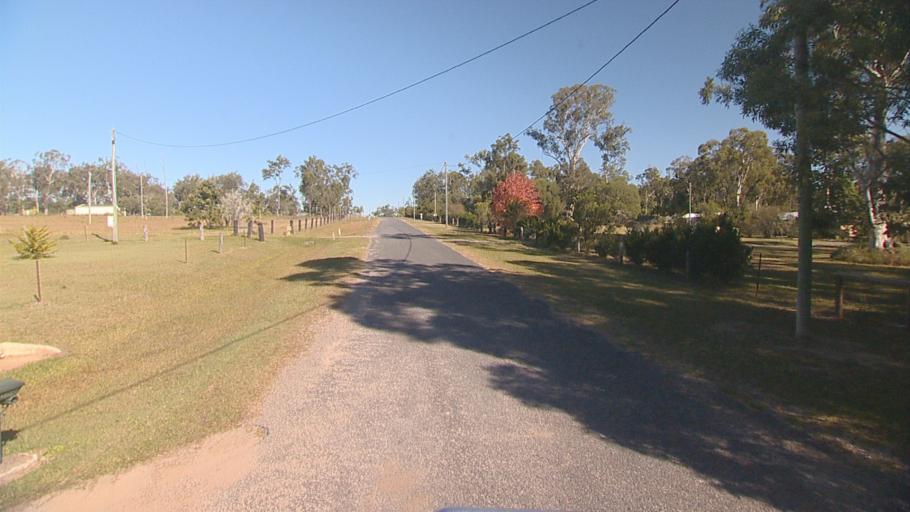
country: AU
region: Queensland
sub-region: Logan
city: Logan Reserve
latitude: -27.7255
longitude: 153.0674
